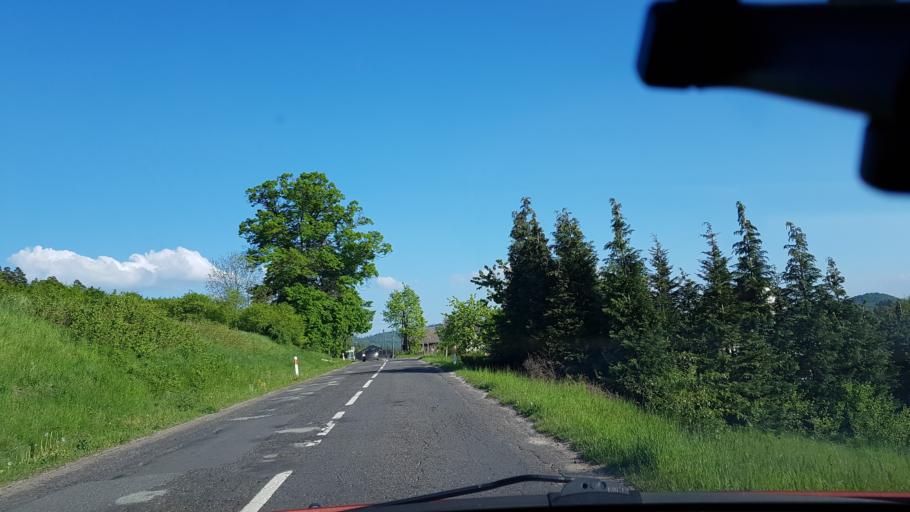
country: PL
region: Lower Silesian Voivodeship
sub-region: Powiat klodzki
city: Bozkow
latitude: 50.5799
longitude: 16.5875
